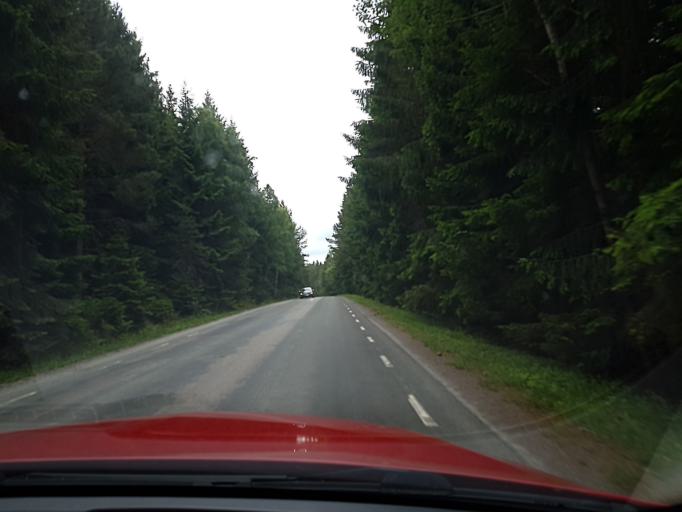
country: SE
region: Vaestra Goetaland
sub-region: Tidaholms Kommun
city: Olofstorp
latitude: 58.3237
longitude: 13.9975
